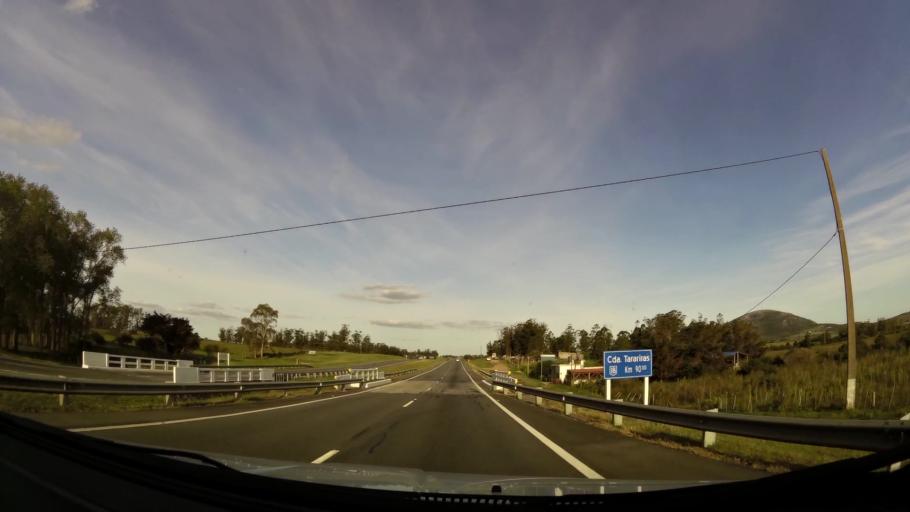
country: UY
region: Maldonado
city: Pan de Azucar
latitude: -34.7898
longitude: -55.3019
